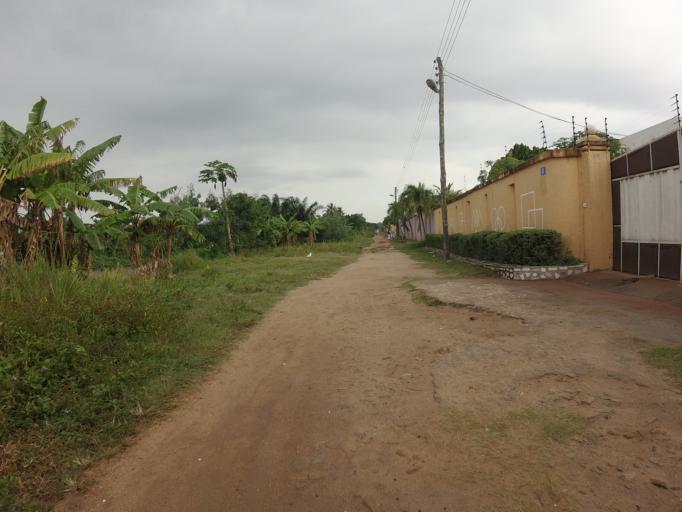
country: GH
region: Greater Accra
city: Dome
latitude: 5.6352
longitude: -0.2310
